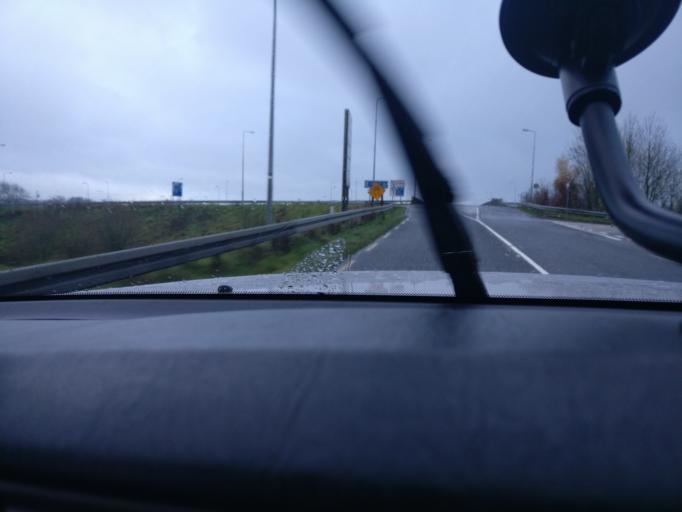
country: IE
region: Leinster
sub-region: An Iarmhi
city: Kinnegad
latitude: 53.4503
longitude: -7.1231
